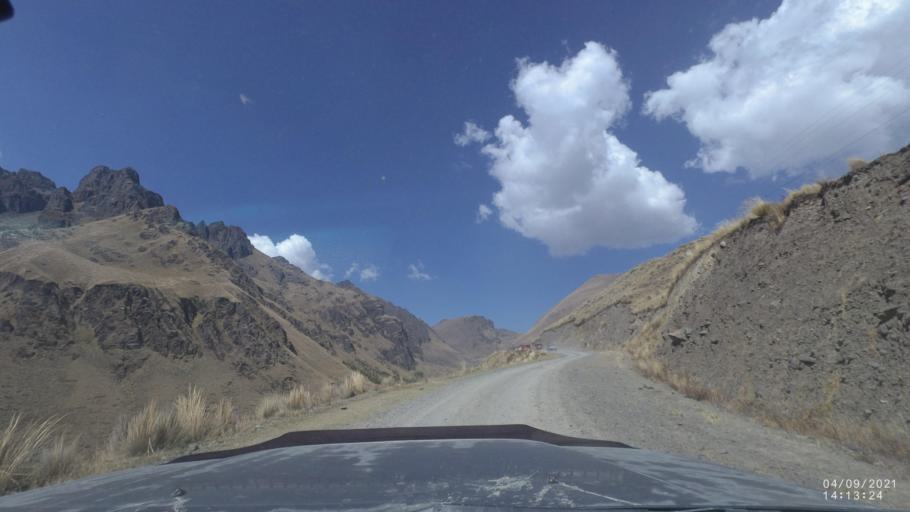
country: BO
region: Cochabamba
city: Sipe Sipe
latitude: -17.2238
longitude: -66.4483
